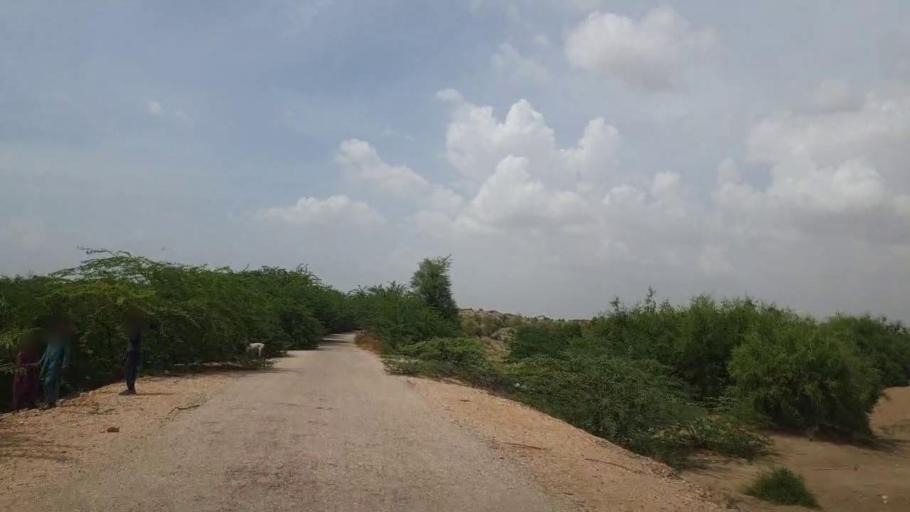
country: PK
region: Sindh
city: Kot Diji
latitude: 27.2464
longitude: 69.0781
